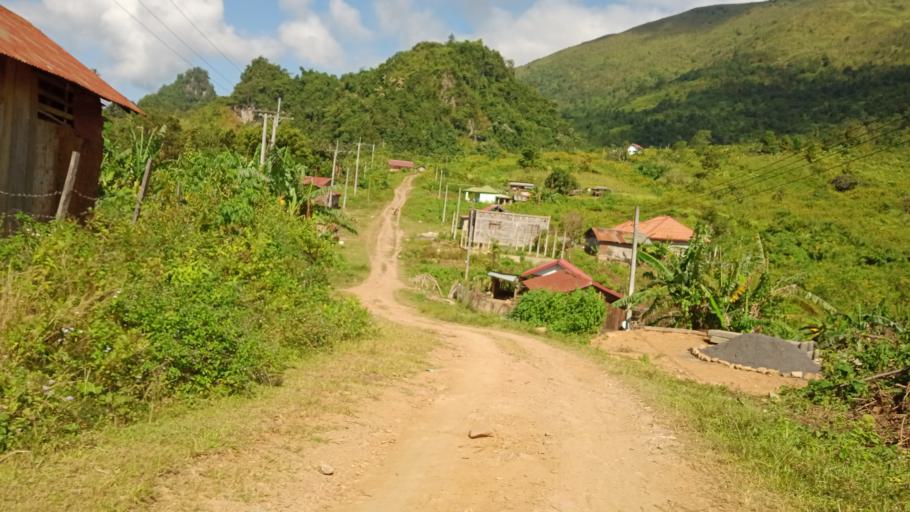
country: LA
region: Xiangkhoang
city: Phonsavan
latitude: 19.1108
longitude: 102.9265
